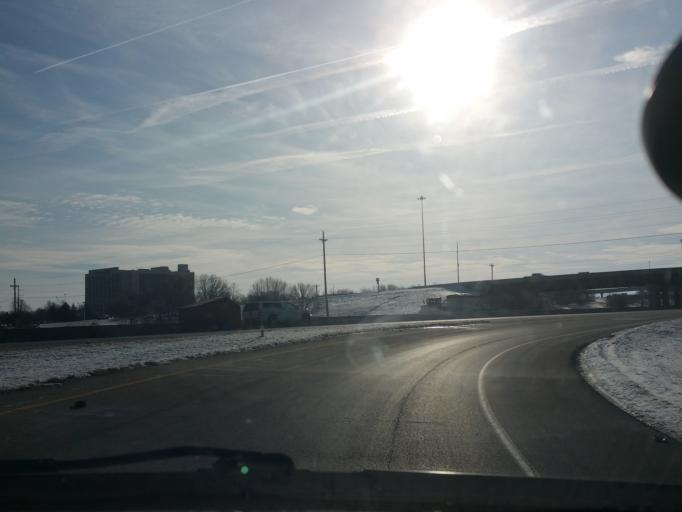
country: US
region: Iowa
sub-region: Polk County
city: Clive
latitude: 41.6019
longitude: -93.7775
